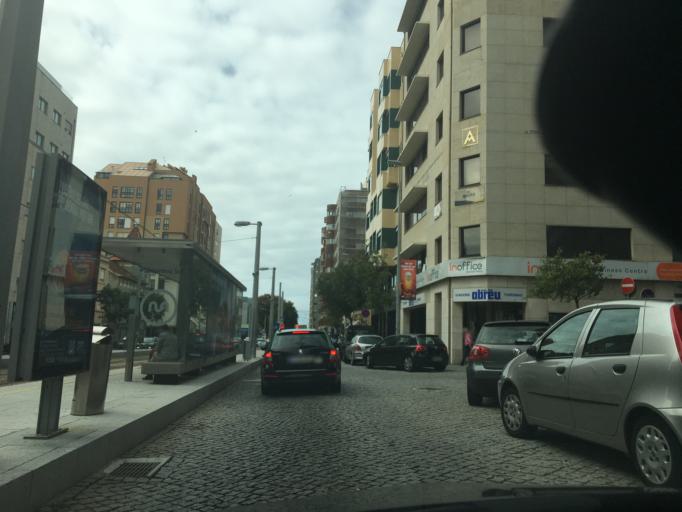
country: PT
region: Porto
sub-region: Matosinhos
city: Matosinhos
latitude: 41.1802
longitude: -8.6883
